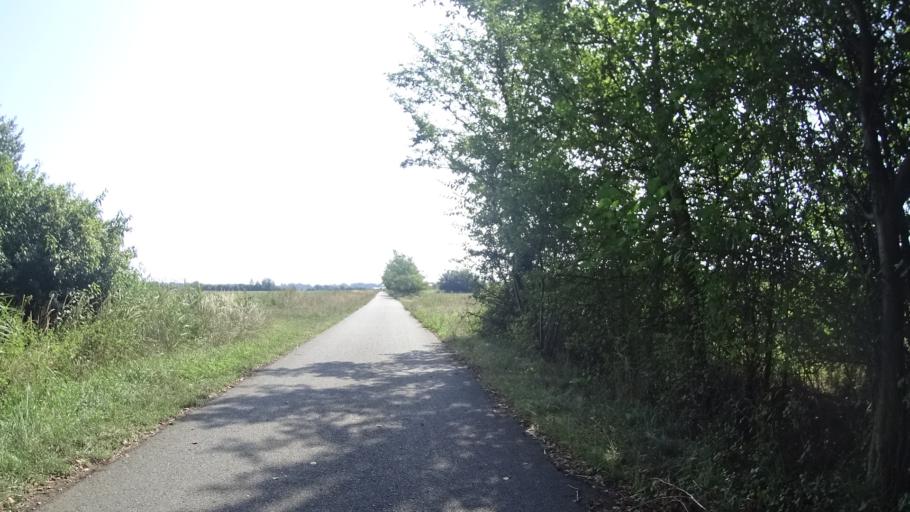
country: DE
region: Brandenburg
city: Burg
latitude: 51.8226
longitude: 14.1613
